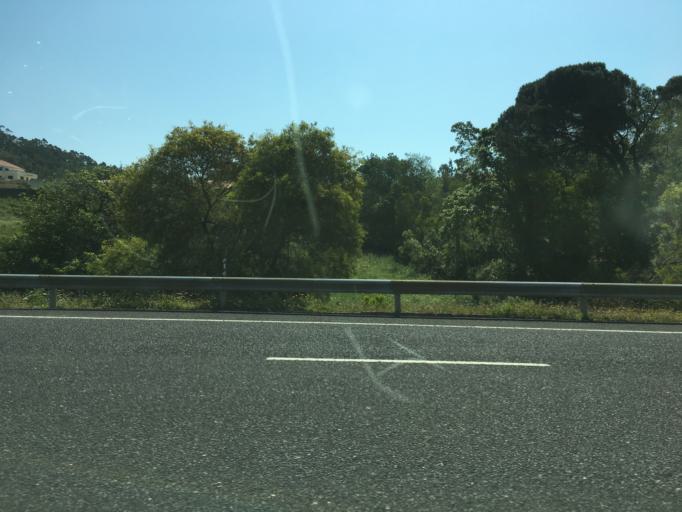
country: PT
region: Lisbon
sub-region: Sintra
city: Belas
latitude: 38.7880
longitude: -9.2401
